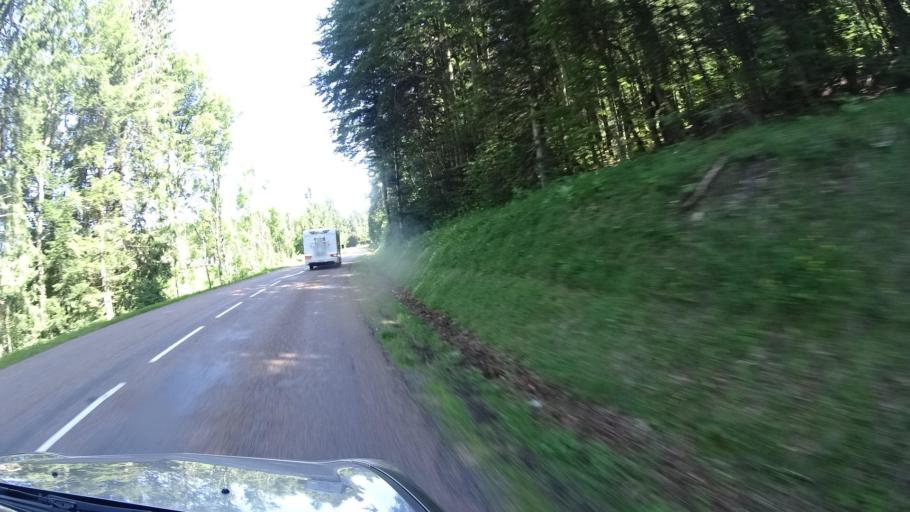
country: FR
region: Franche-Comte
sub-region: Departement du Jura
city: Longchaumois
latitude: 46.5052
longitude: 5.8993
